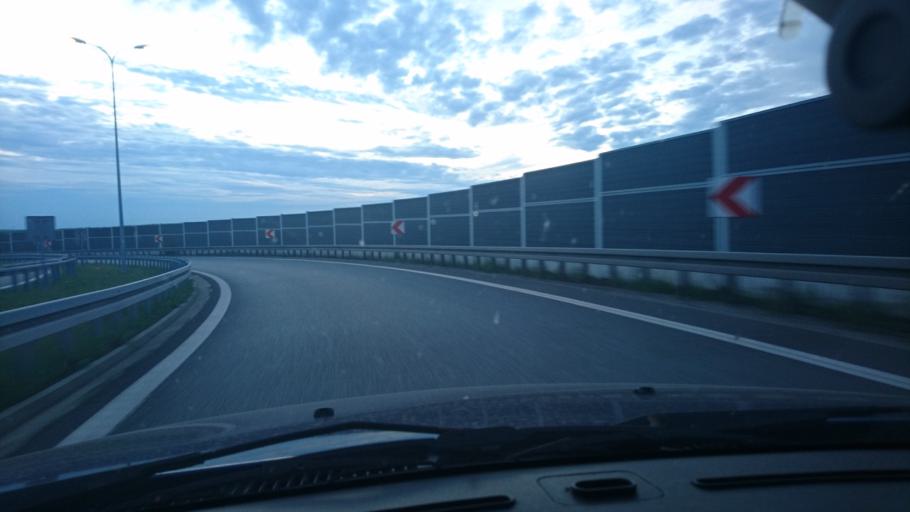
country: PL
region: Silesian Voivodeship
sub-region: Powiat tarnogorski
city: Wieszowa
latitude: 50.3758
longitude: 18.7716
